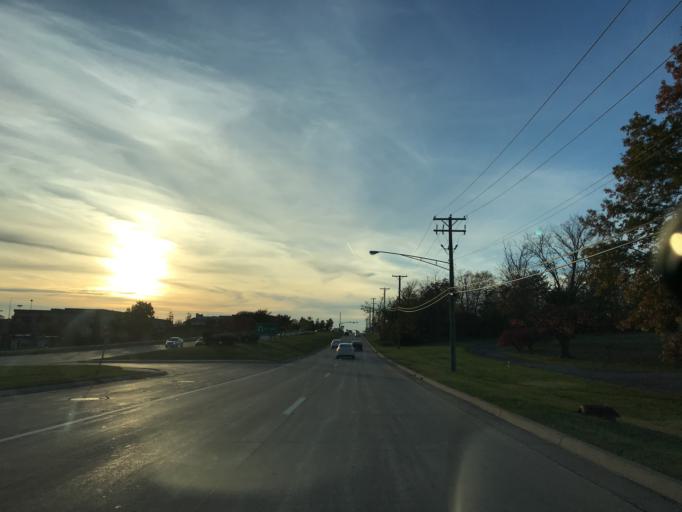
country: US
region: Michigan
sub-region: Oakland County
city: Novi
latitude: 42.4959
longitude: -83.4697
